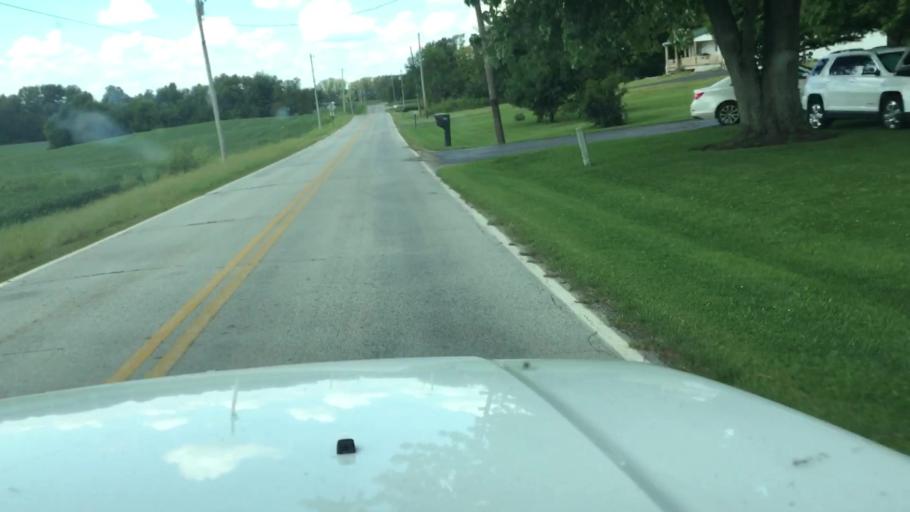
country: US
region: Ohio
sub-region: Madison County
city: Choctaw Lake
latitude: 39.9314
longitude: -83.5642
